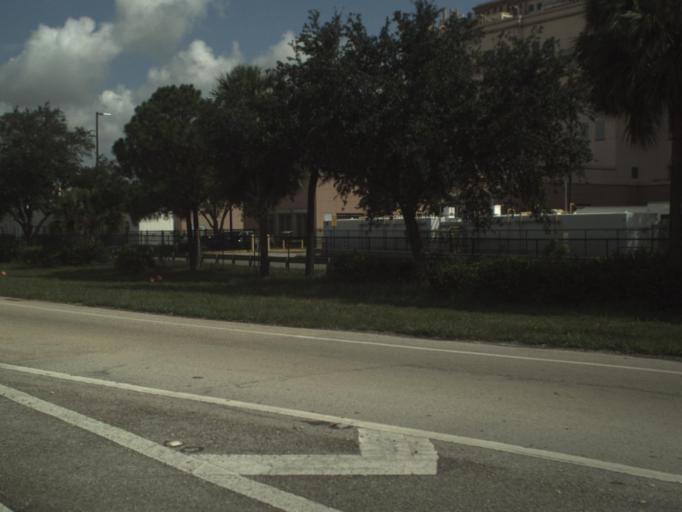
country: US
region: Florida
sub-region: Palm Beach County
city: Mangonia Park
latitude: 26.7838
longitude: -80.1131
